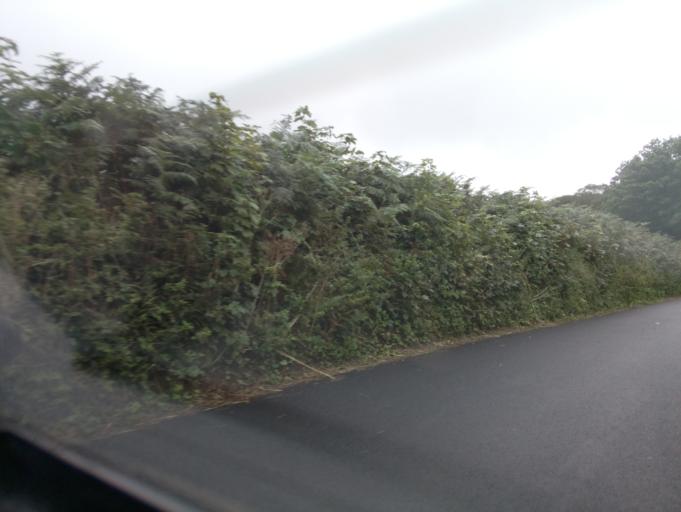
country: GB
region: England
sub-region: Devon
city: Totnes
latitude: 50.3543
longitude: -3.6611
